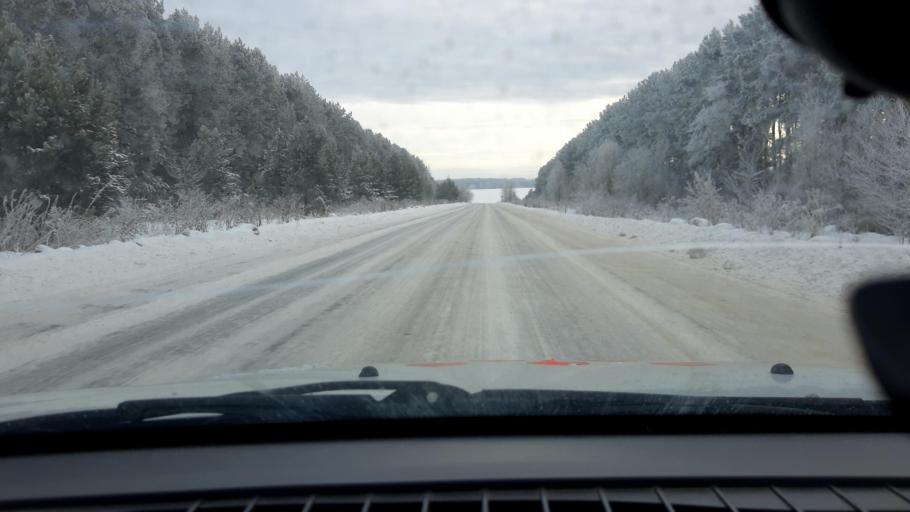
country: RU
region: Nizjnij Novgorod
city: Bogorodsk
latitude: 56.0860
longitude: 43.5649
